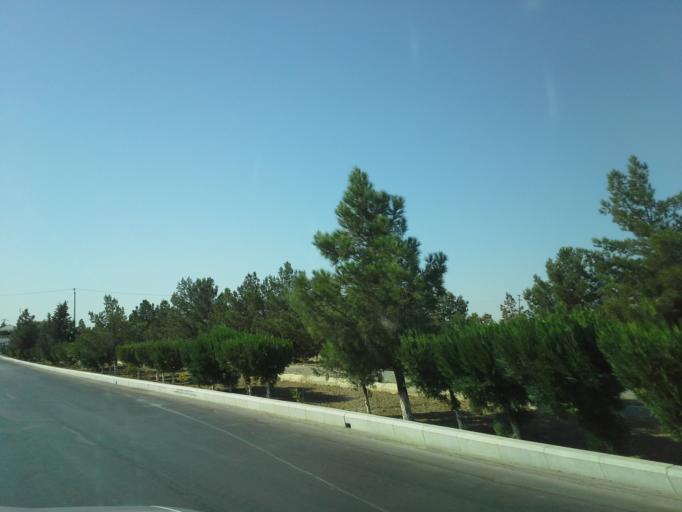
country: TM
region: Ahal
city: Annau
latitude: 37.9198
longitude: 58.4504
